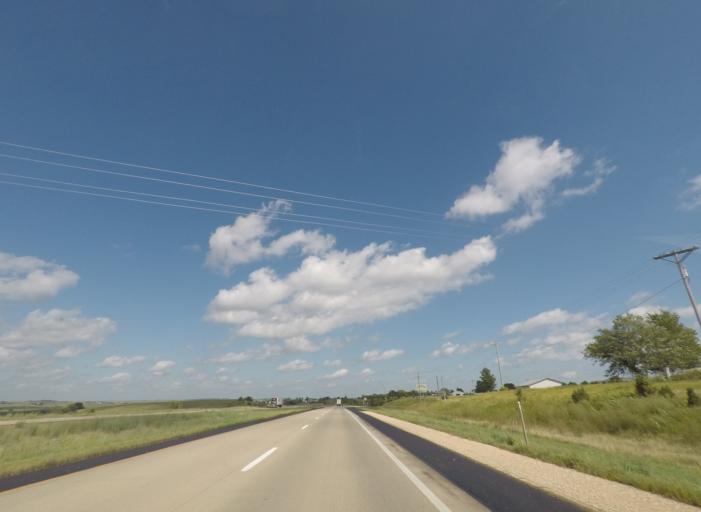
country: US
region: Iowa
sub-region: Dubuque County
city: Cascade
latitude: 42.2946
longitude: -91.0436
